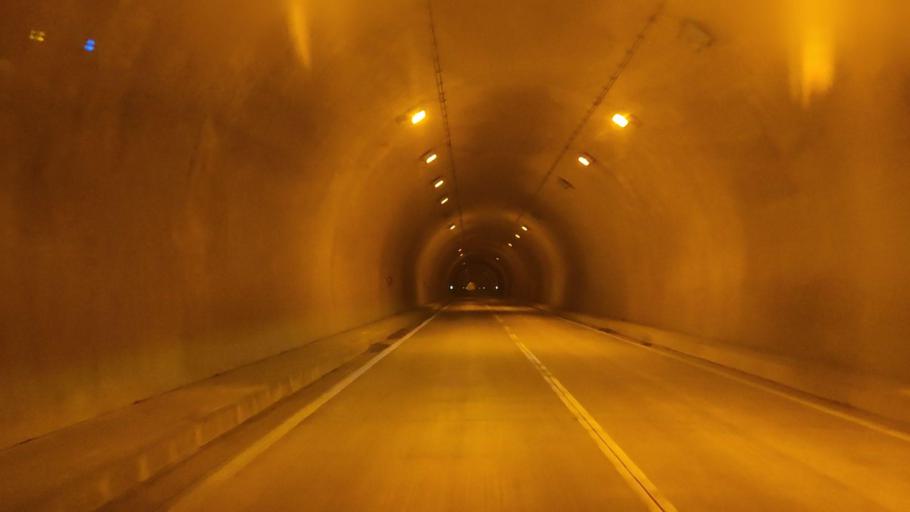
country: JP
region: Kumamoto
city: Matsubase
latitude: 32.5083
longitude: 130.9210
